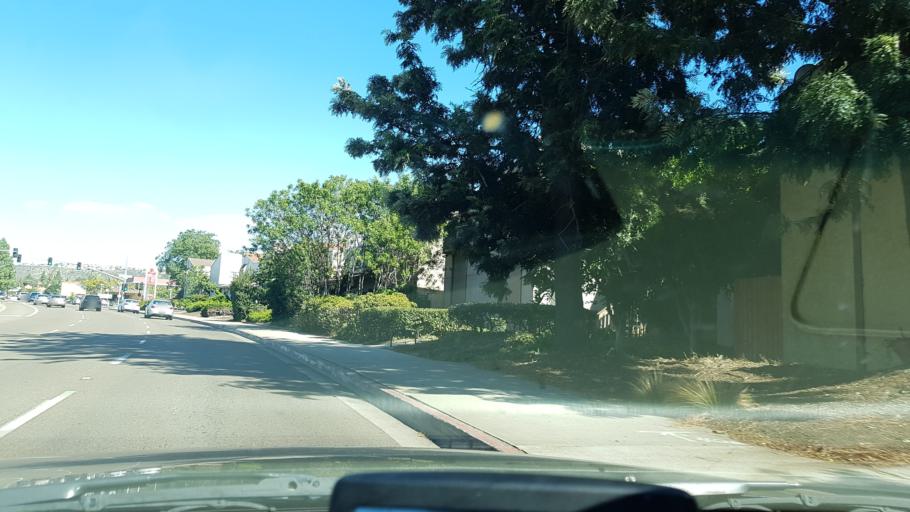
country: US
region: California
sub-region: San Diego County
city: Fairbanks Ranch
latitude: 32.9131
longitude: -117.1339
